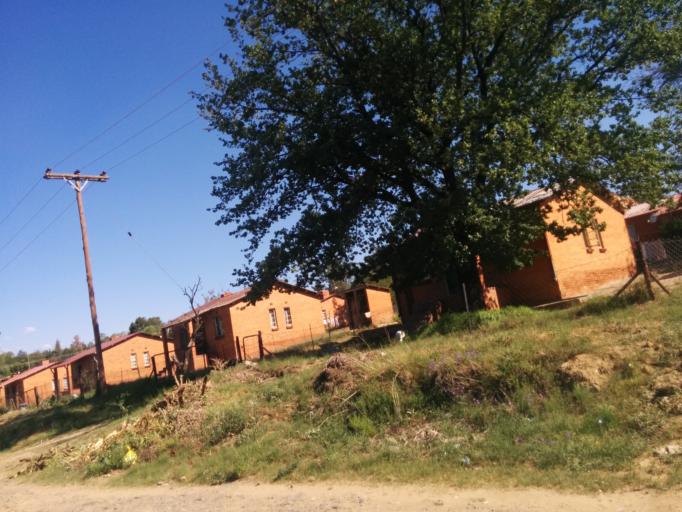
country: LS
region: Maseru
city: Maseru
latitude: -29.3004
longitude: 27.4649
